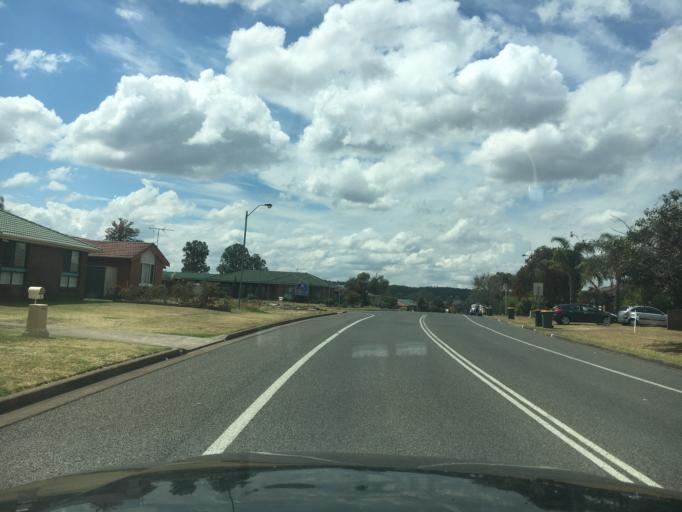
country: AU
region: New South Wales
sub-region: Singleton
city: Singleton
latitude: -32.5446
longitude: 151.1732
